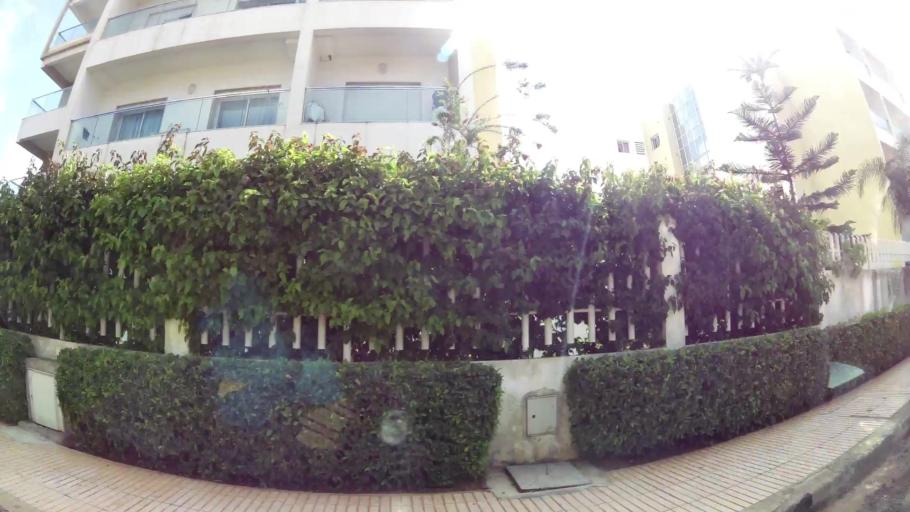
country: MA
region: Rabat-Sale-Zemmour-Zaer
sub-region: Skhirate-Temara
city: Temara
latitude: 33.9484
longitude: -6.8784
